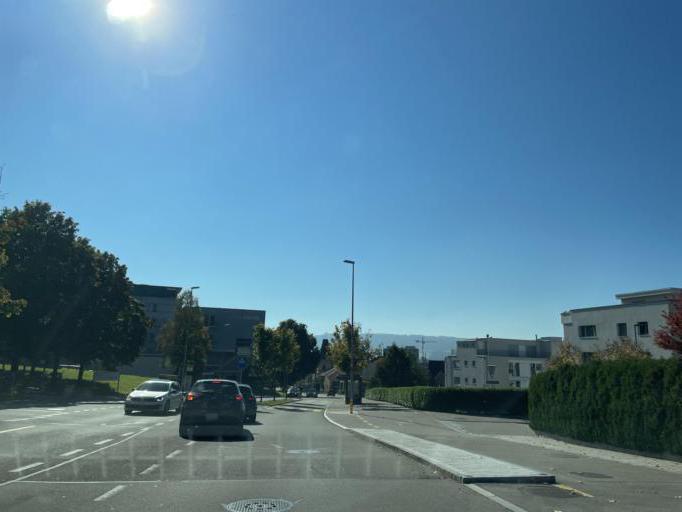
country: CH
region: Zurich
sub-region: Bezirk Uster
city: Uster
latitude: 47.3545
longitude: 8.7239
